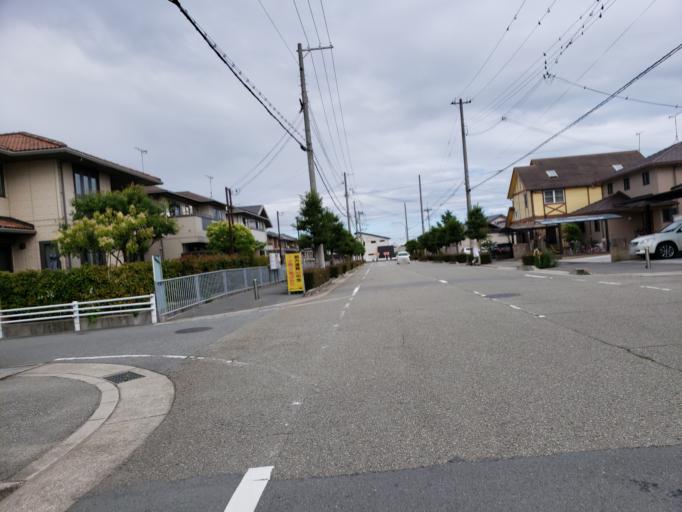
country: JP
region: Hyogo
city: Kakogawacho-honmachi
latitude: 34.7479
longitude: 134.8198
